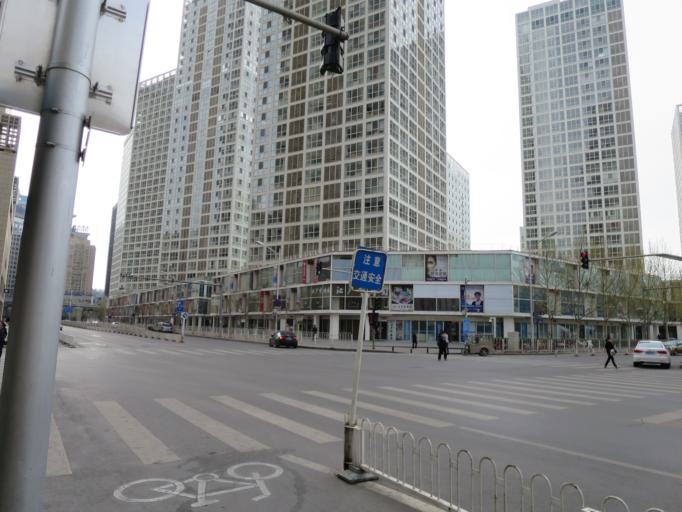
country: CN
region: Beijing
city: Chaowai
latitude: 39.9053
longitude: 116.4512
